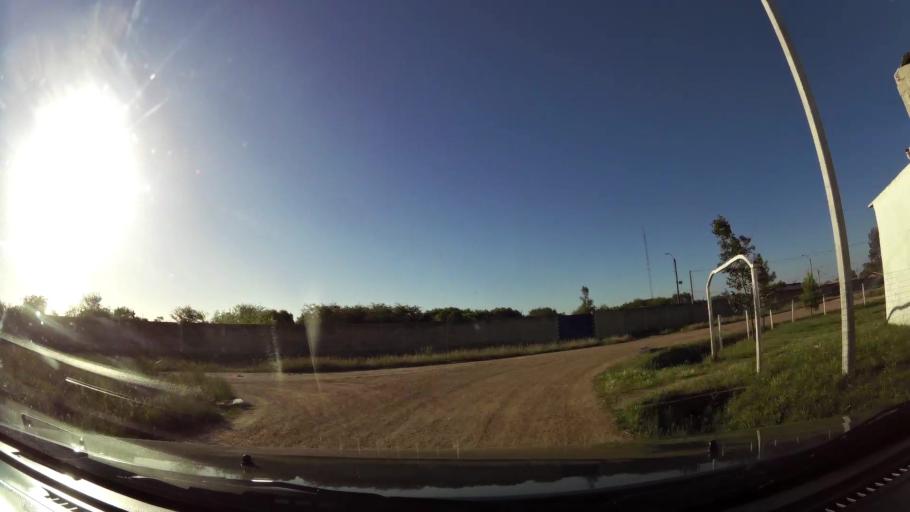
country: UY
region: Canelones
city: Paso de Carrasco
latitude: -34.8570
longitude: -56.0542
